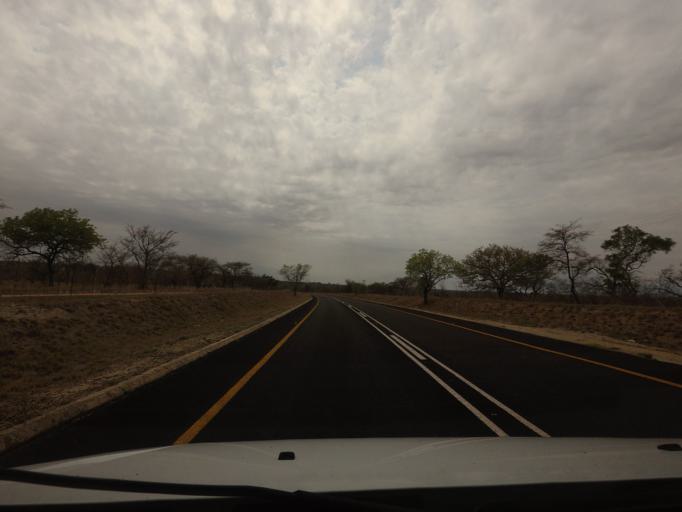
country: ZA
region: Limpopo
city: Thulamahashi
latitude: -24.5599
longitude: 31.1736
